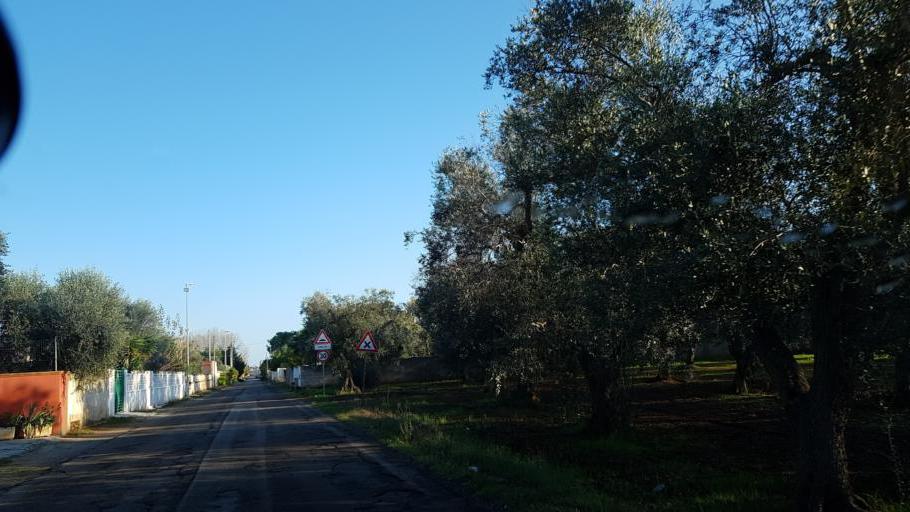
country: IT
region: Apulia
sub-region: Provincia di Brindisi
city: Torchiarolo
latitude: 40.5031
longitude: 18.1089
